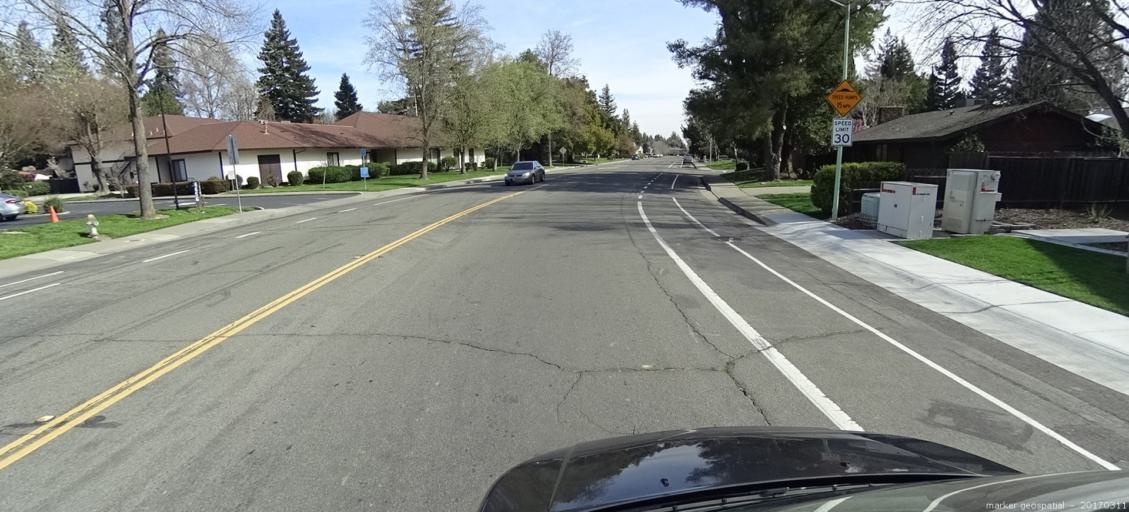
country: US
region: California
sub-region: Yolo County
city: West Sacramento
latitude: 38.5061
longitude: -121.5499
